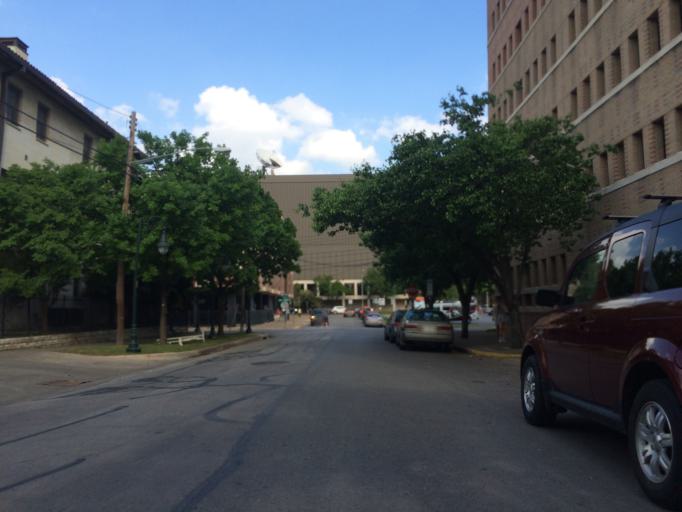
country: US
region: Texas
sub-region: Travis County
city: Austin
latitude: 30.2892
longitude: -97.7428
